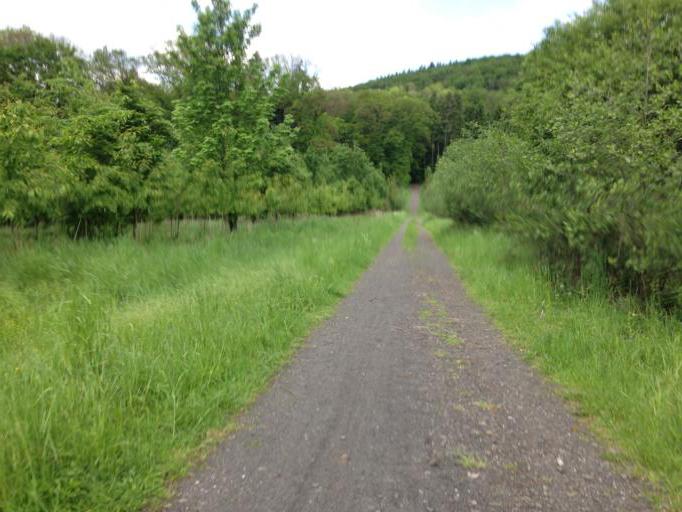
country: DE
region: Hesse
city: Lollar
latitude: 50.6357
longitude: 8.7157
